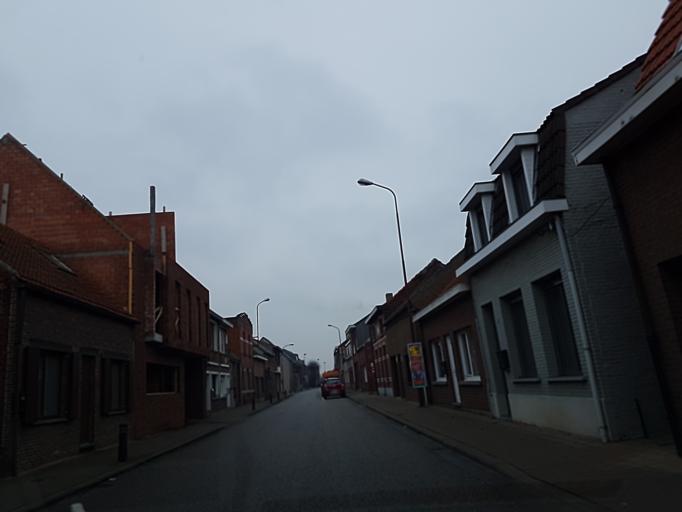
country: BE
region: Flanders
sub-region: Provincie Antwerpen
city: Stabroek
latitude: 51.3304
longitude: 4.3681
